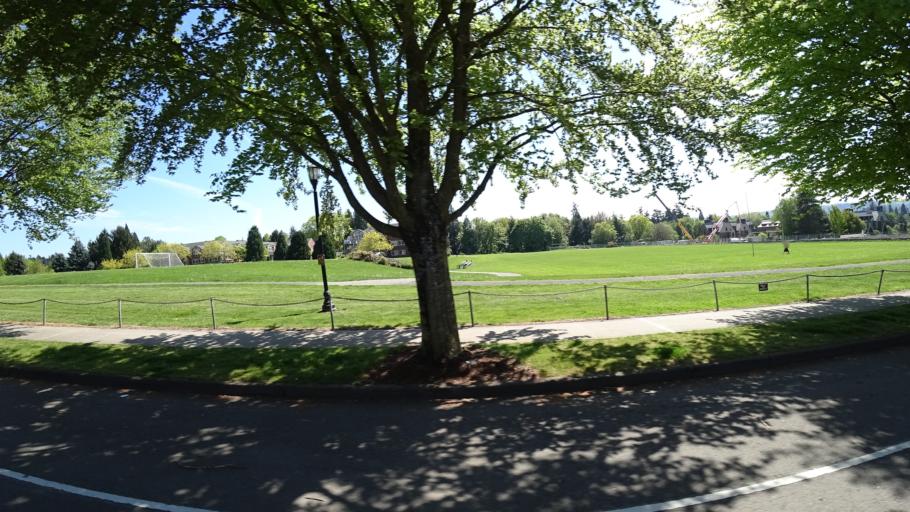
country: US
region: Oregon
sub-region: Clackamas County
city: Milwaukie
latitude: 45.4847
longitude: -122.6329
